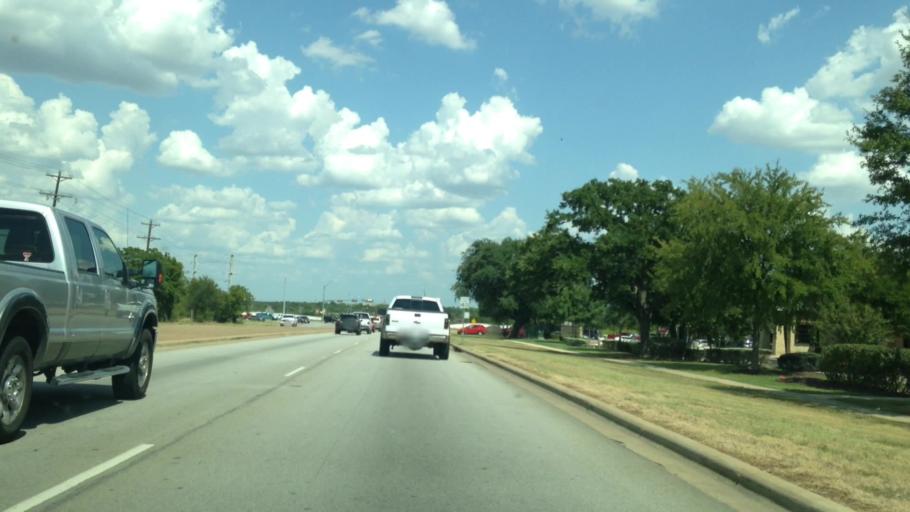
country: US
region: Texas
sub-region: Williamson County
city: Georgetown
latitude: 30.6329
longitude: -97.6948
